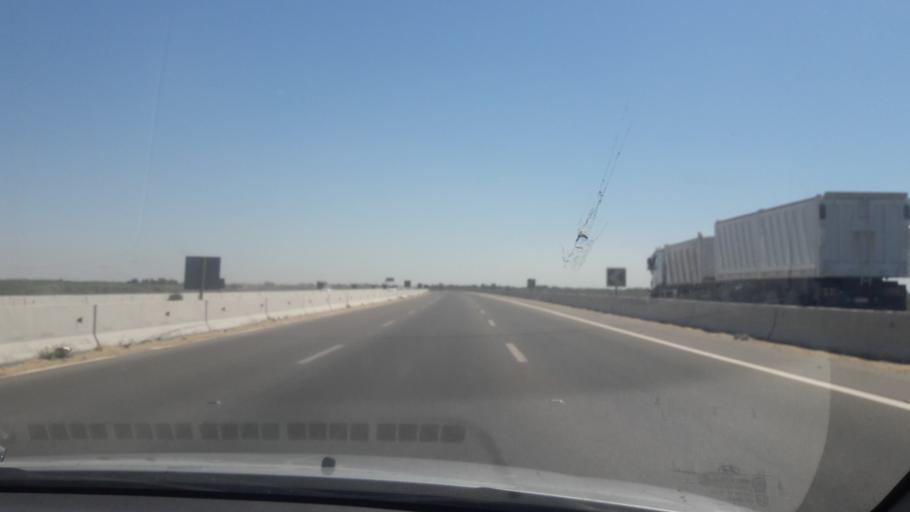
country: EG
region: Al Isma'iliyah
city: Ismailia
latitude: 30.8994
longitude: 32.1801
